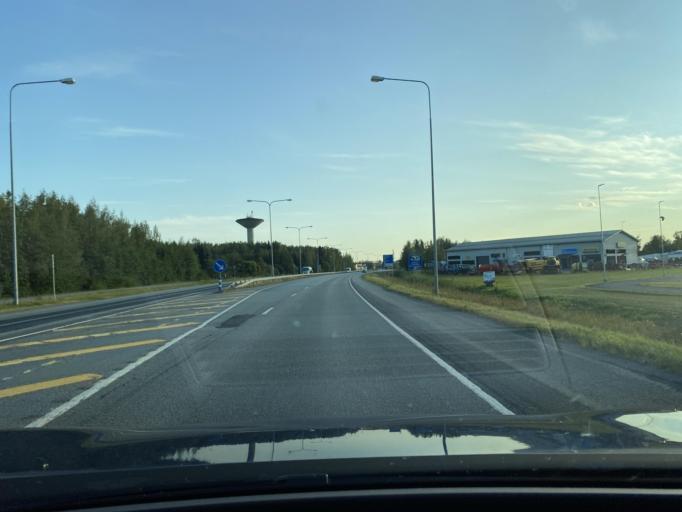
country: FI
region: Southern Ostrobothnia
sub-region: Seinaejoki
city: Nurmo
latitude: 62.8107
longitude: 22.8902
